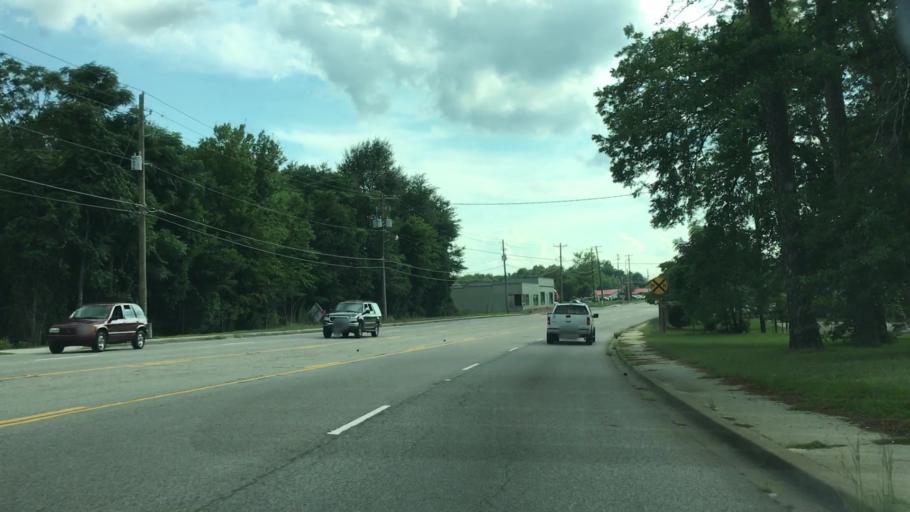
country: US
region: South Carolina
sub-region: Aiken County
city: Aiken
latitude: 33.5719
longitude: -81.7070
